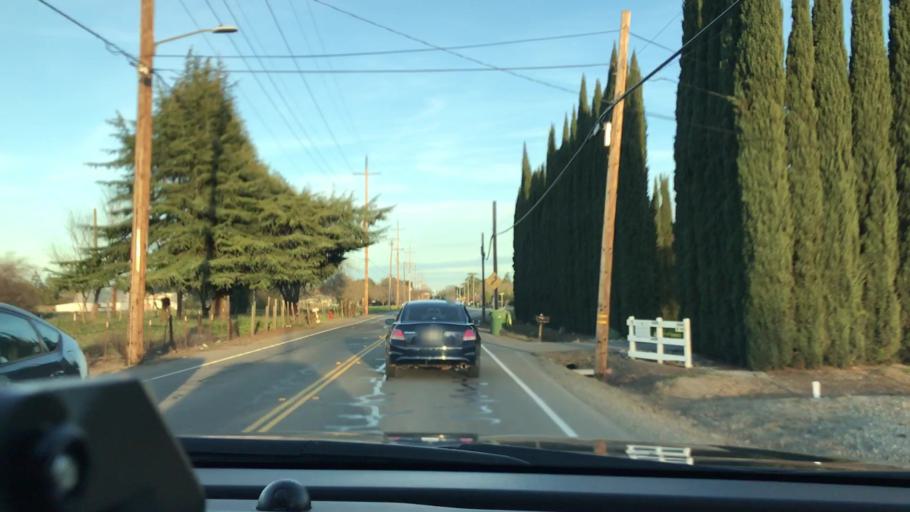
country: US
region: California
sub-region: Contra Costa County
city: Brentwood
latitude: 37.9616
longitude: -121.7102
